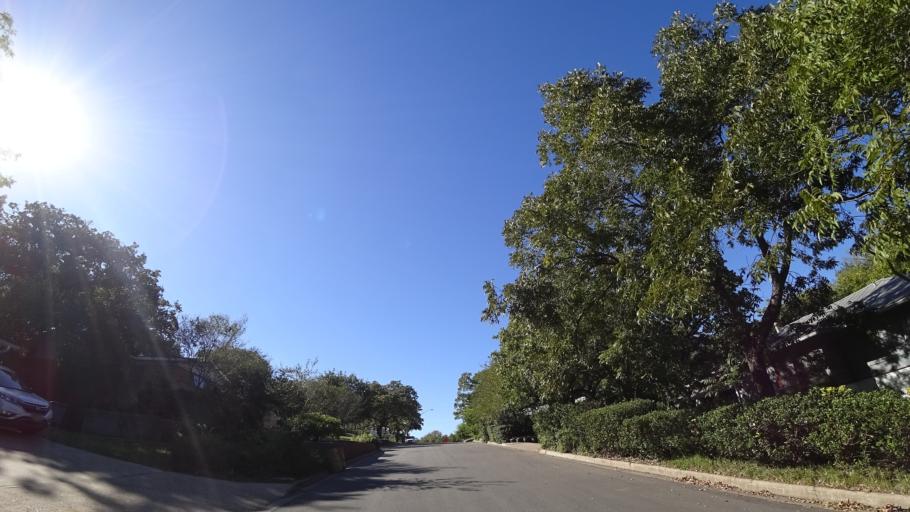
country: US
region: Texas
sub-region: Travis County
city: Austin
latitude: 30.2436
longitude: -97.7316
